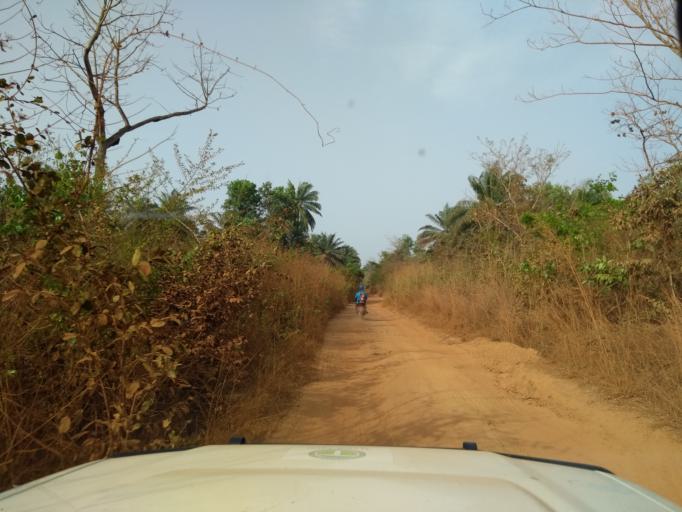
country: GN
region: Kindia
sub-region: Prefecture de Dubreka
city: Dubreka
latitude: 9.8476
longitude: -13.5577
